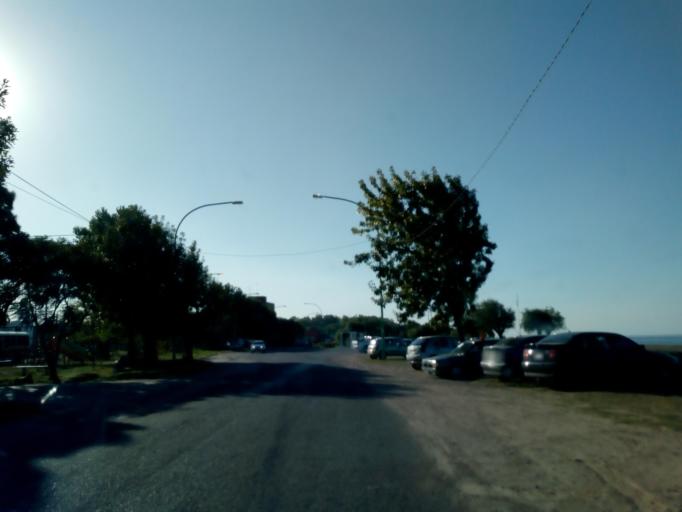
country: AR
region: Buenos Aires
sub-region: Partido de Ensenada
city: Ensenada
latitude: -34.8070
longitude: -57.9829
